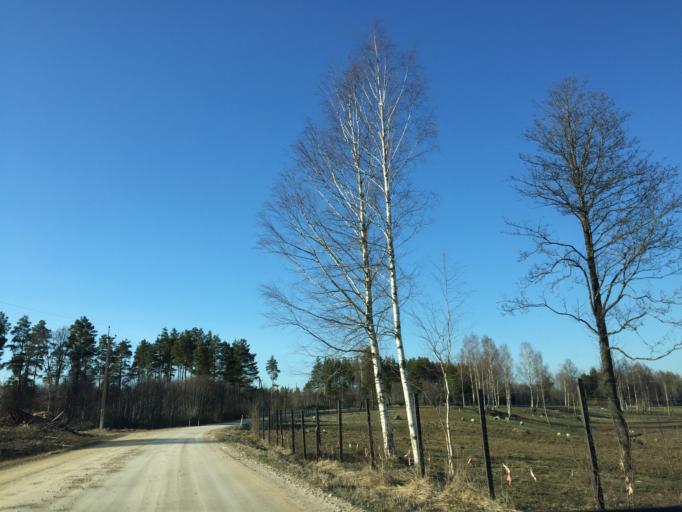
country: EE
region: Ida-Virumaa
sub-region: Sillamaee linn
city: Sillamae
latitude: 59.1279
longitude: 27.8018
